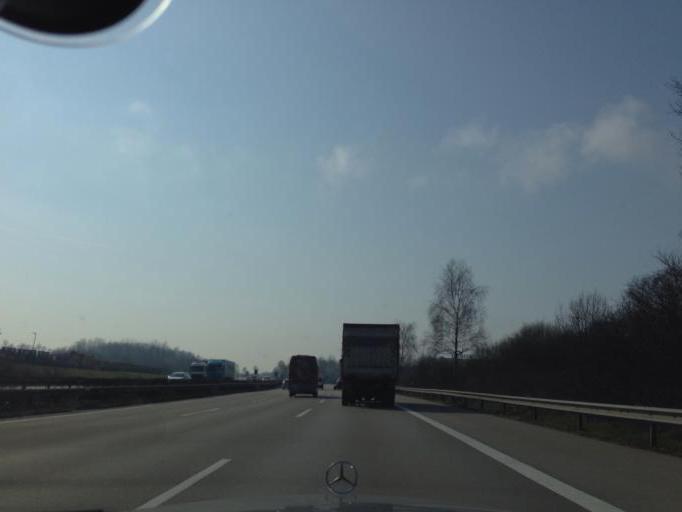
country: DE
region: Schleswig-Holstein
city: Braak
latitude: 53.6201
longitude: 10.2355
